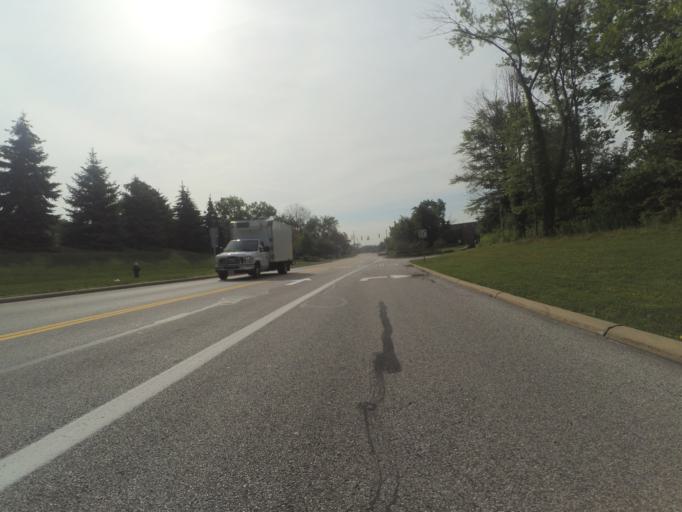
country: US
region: Ohio
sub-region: Cuyahoga County
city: Orange
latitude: 41.4649
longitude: -81.4839
